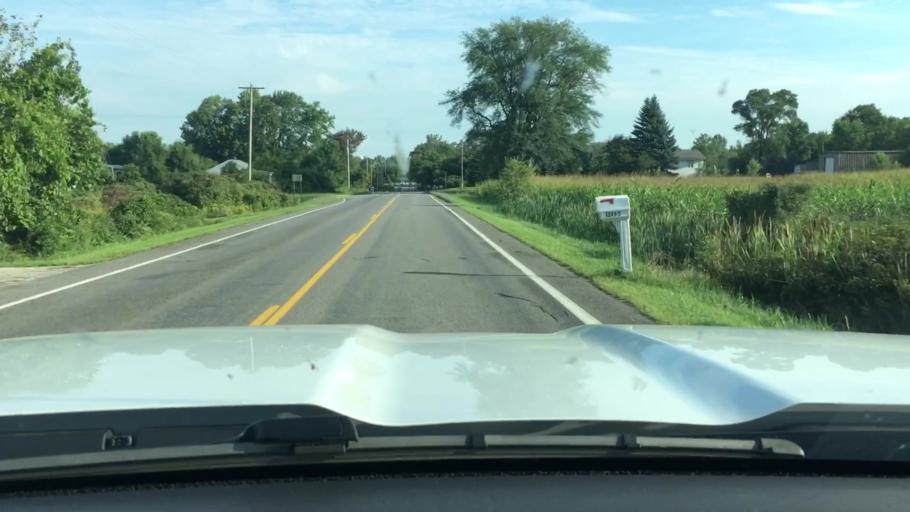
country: US
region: Michigan
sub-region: Kent County
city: Kent City
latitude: 43.2040
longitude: -85.7708
